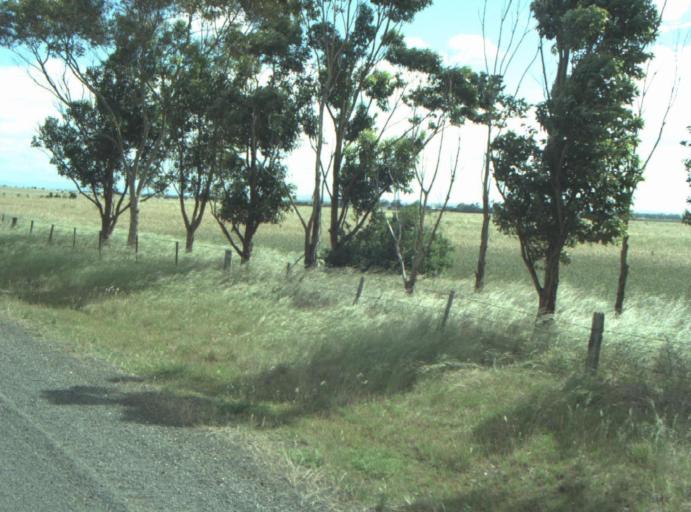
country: AU
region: Victoria
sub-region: Greater Geelong
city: Lara
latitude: -37.8866
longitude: 144.3202
